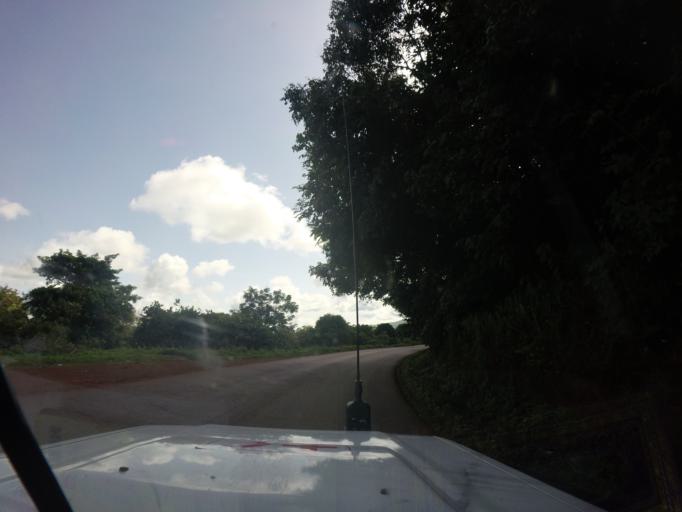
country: GN
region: Mamou
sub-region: Mamou Prefecture
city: Mamou
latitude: 10.3514
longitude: -12.2043
